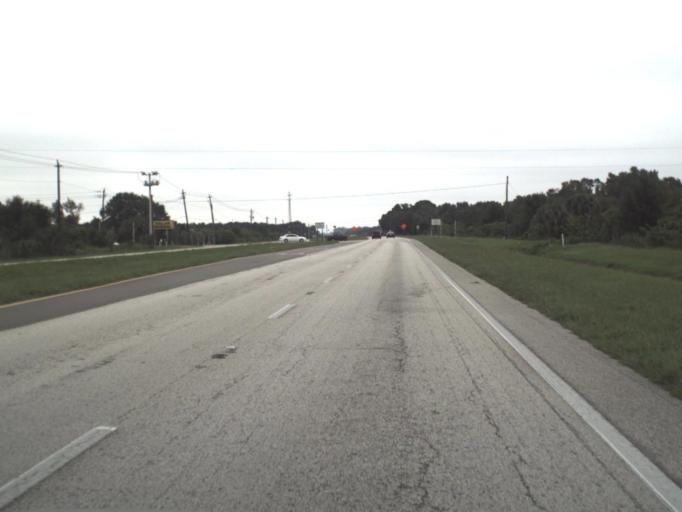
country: US
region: Florida
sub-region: Manatee County
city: Memphis
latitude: 27.5952
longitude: -82.5396
